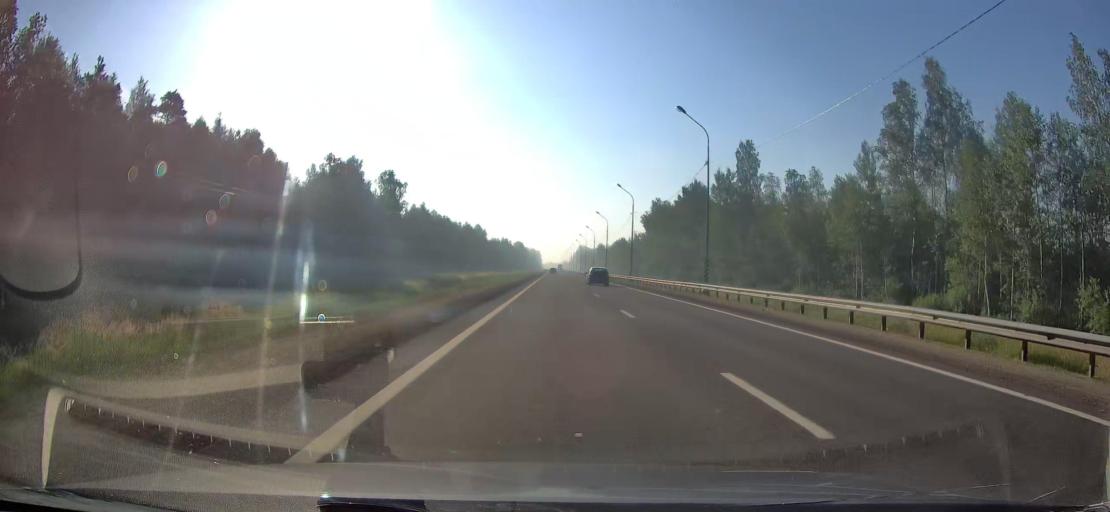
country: RU
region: Leningrad
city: Sinyavino
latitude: 59.8935
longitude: 31.1373
